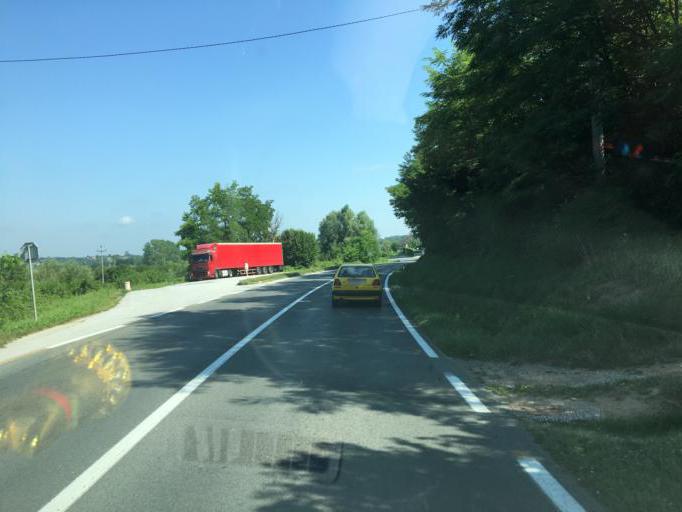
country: HR
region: Karlovacka
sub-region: Grad Karlovac
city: Karlovac
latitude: 45.4184
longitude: 15.6066
